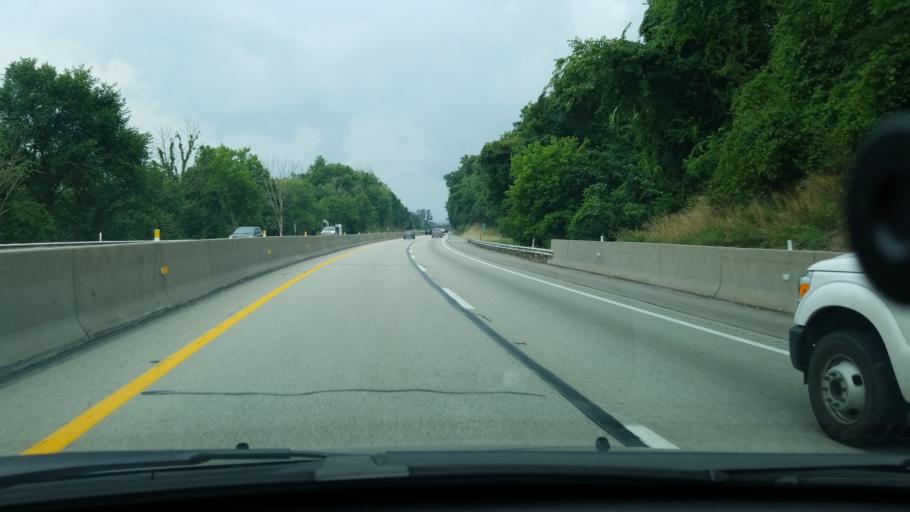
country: US
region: Pennsylvania
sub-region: Allegheny County
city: Plum
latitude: 40.4823
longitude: -79.7712
